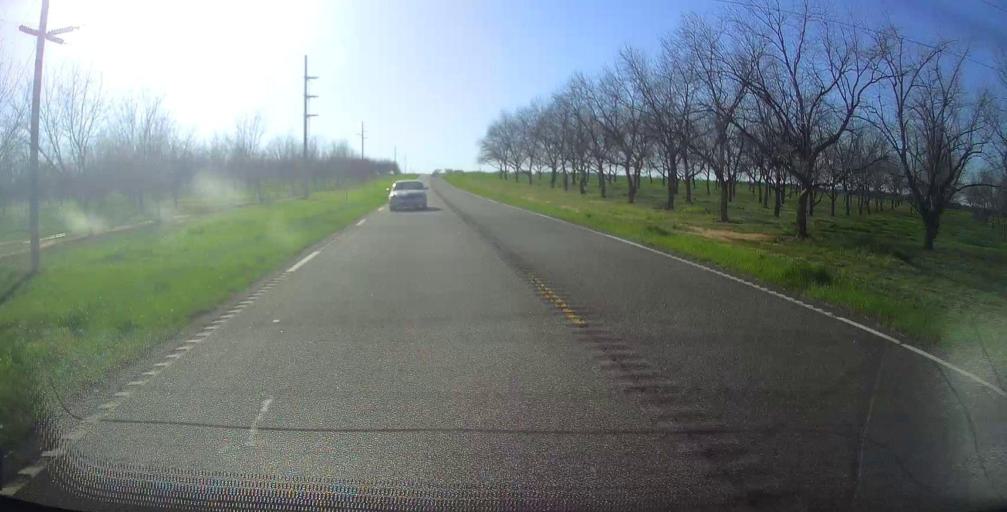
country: US
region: Georgia
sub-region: Macon County
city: Marshallville
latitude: 32.4395
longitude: -83.8681
